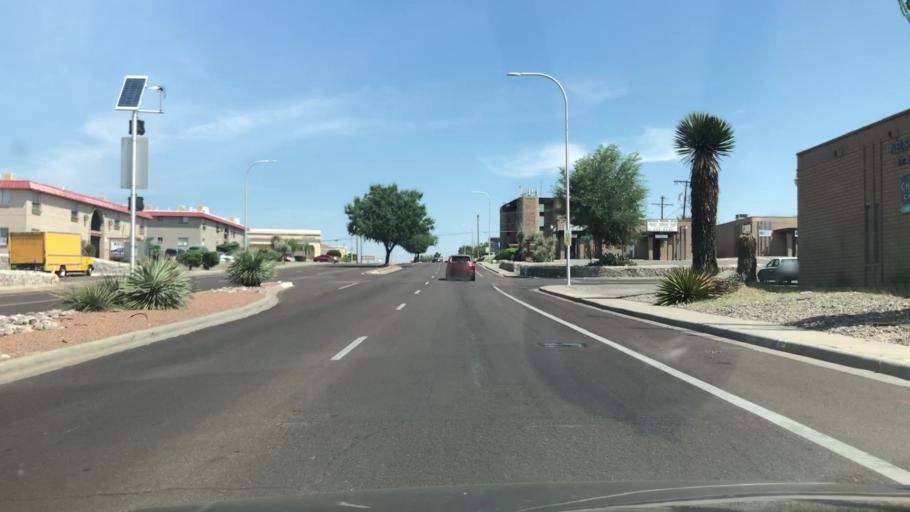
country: US
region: New Mexico
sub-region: Dona Ana County
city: University Park
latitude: 32.3038
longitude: -106.7378
